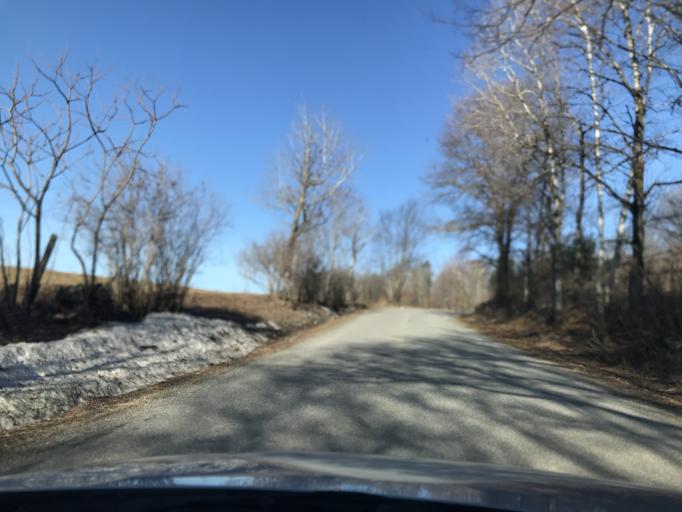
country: US
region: Wisconsin
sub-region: Marinette County
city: Niagara
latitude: 45.3806
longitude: -88.0374
